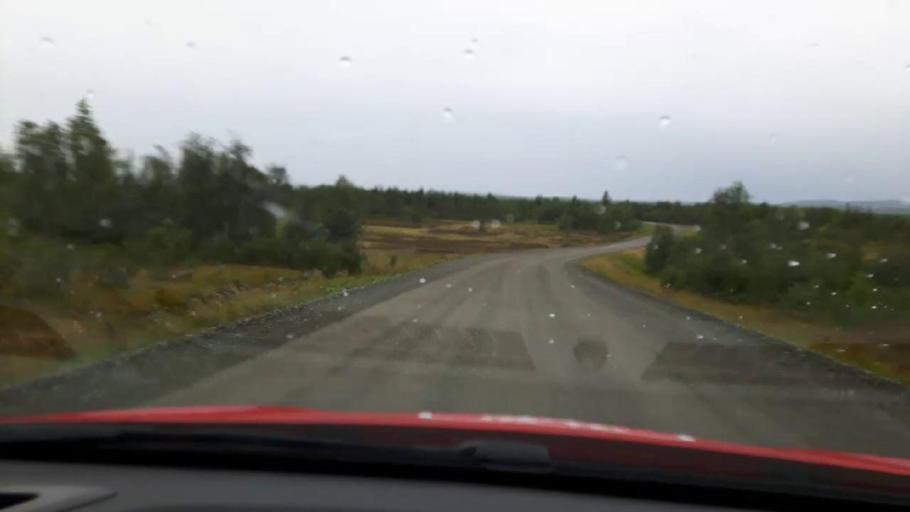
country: NO
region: Nord-Trondelag
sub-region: Meraker
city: Meraker
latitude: 63.5850
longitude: 12.2679
